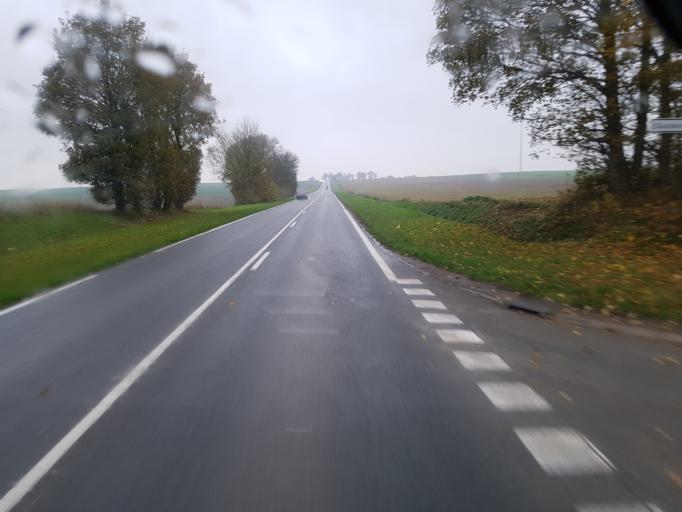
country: FR
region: Picardie
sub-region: Departement de l'Aisne
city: Omissy
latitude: 49.8986
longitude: 3.2624
